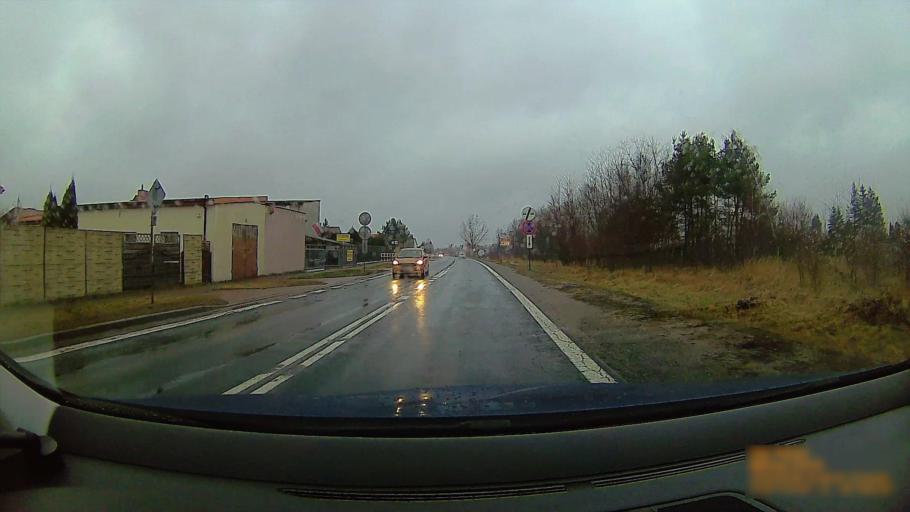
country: PL
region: Greater Poland Voivodeship
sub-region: Konin
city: Konin
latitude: 52.1833
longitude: 18.2690
